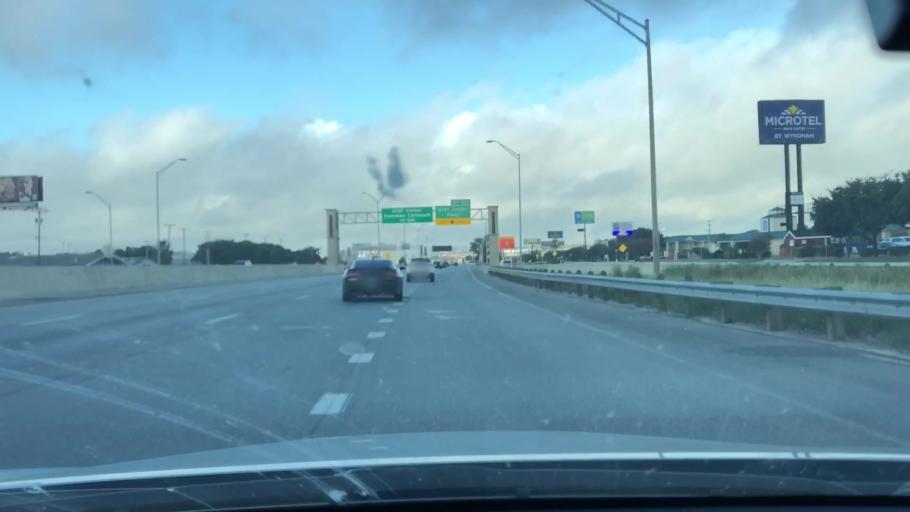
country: US
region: Texas
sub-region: Bexar County
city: Kirby
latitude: 29.4525
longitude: -98.4178
